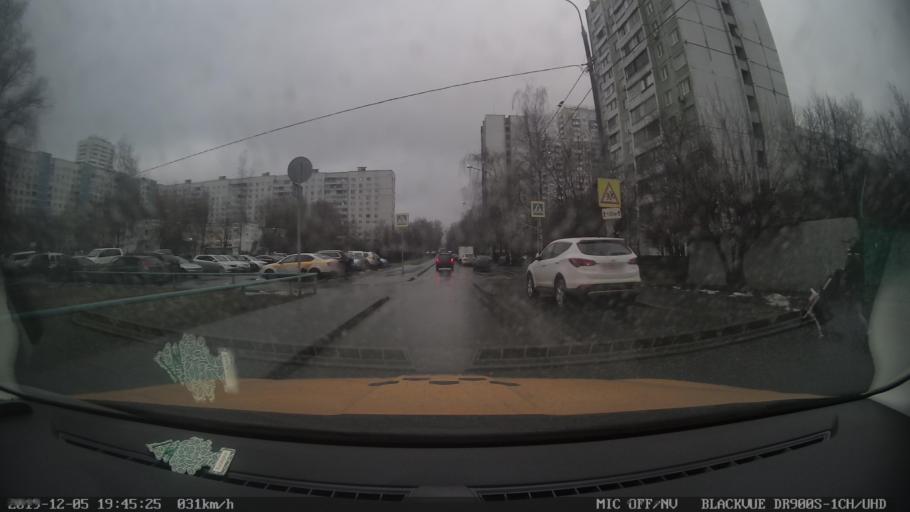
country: RU
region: Moscow
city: Lianozovo
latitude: 55.9036
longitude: 37.5775
